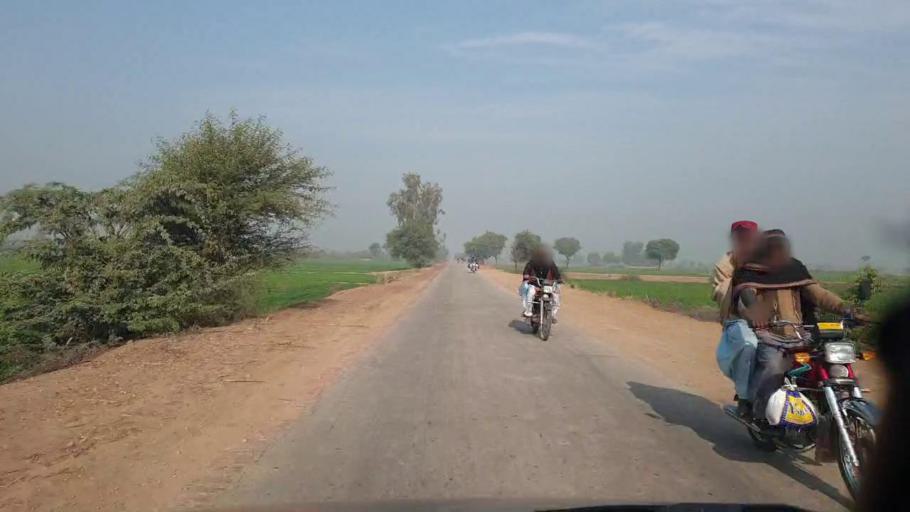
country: PK
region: Sindh
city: Shahdadpur
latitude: 25.9611
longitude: 68.5858
